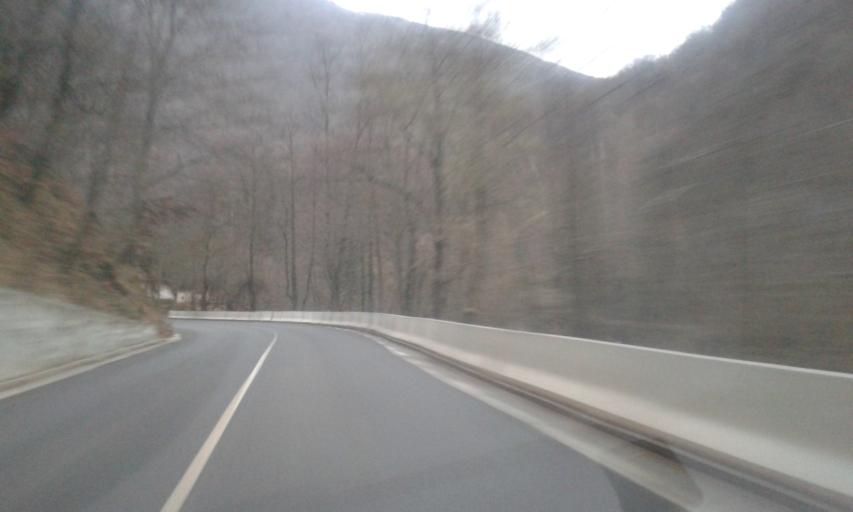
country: RO
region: Gorj
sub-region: Comuna Bumbesti-Jiu
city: Bumbesti-Jiu
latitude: 45.2538
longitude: 23.3861
